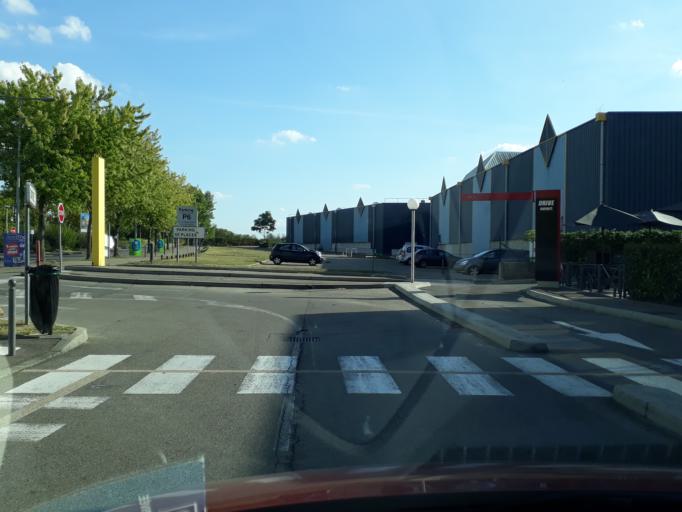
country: FR
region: Rhone-Alpes
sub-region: Departement du Rhone
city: Bron
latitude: 45.7216
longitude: 4.9196
